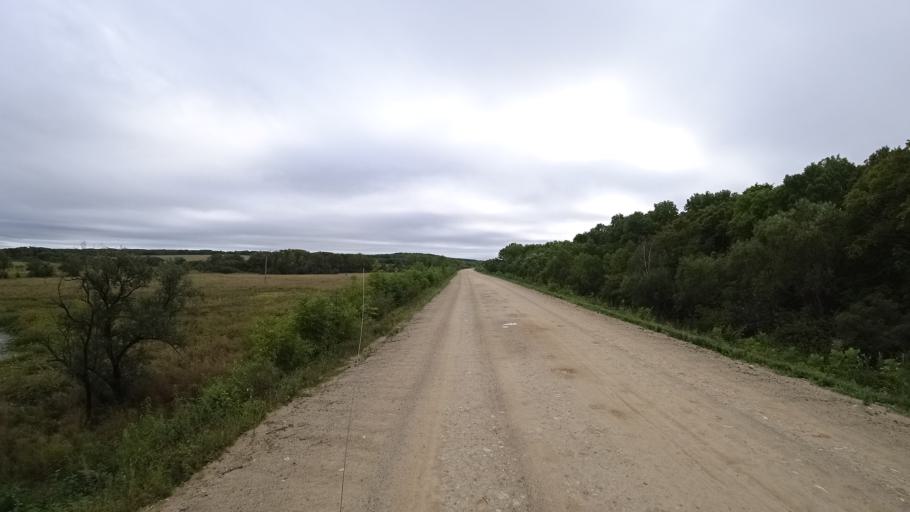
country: RU
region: Primorskiy
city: Rettikhovka
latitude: 44.1254
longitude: 132.6394
